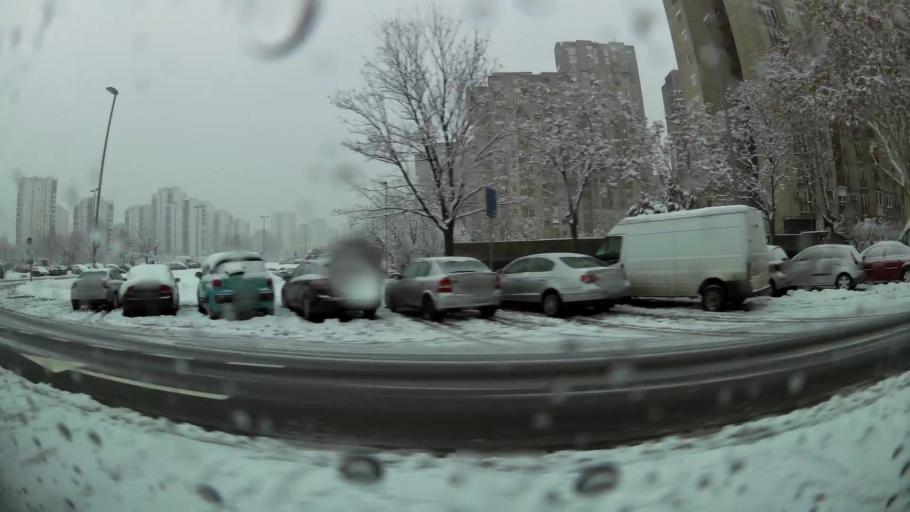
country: RS
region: Central Serbia
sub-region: Belgrade
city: Zemun
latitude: 44.8019
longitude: 20.3747
